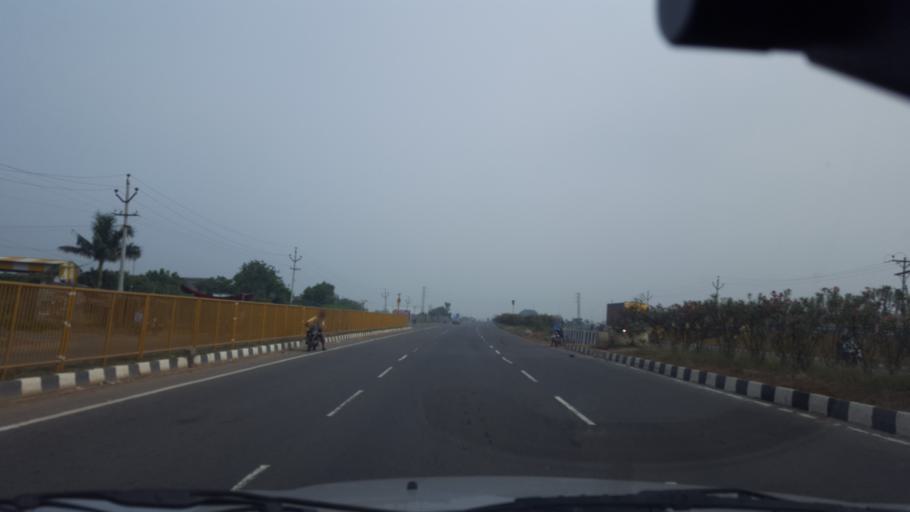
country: IN
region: Andhra Pradesh
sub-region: Guntur
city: Chilakalurupet
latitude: 16.0052
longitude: 80.1138
